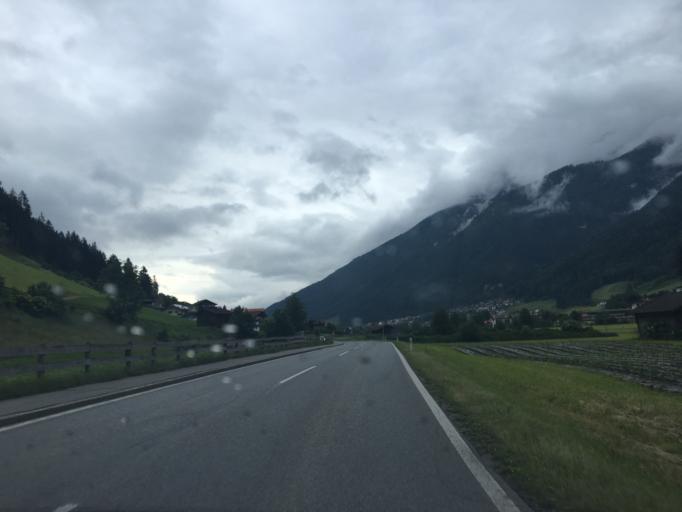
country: AT
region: Tyrol
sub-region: Politischer Bezirk Innsbruck Land
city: Neustift im Stubaital
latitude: 47.1174
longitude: 11.3160
